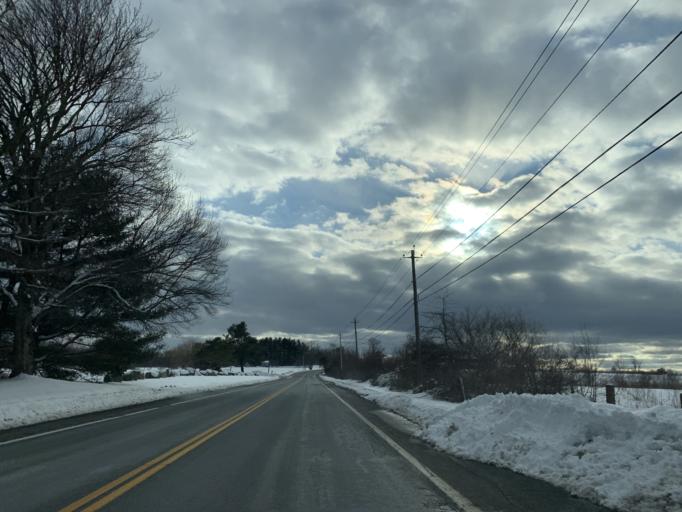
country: US
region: Rhode Island
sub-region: Providence County
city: Cumberland Hill
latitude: 42.0091
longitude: -71.4478
